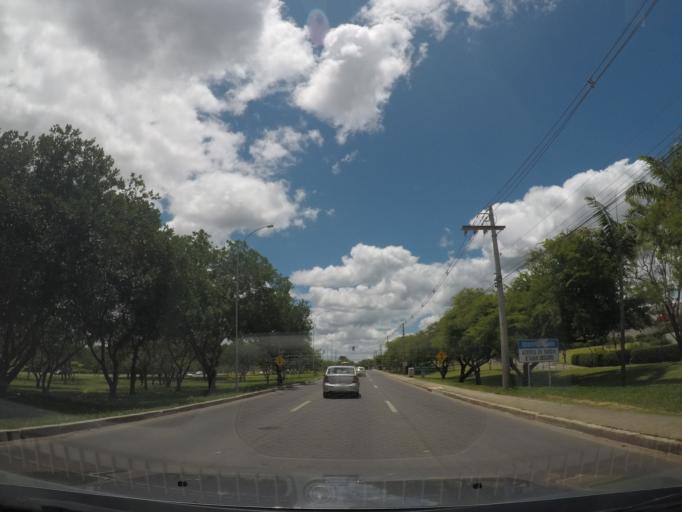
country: BR
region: Federal District
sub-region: Brasilia
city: Brasilia
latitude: -15.7221
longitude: -47.8848
